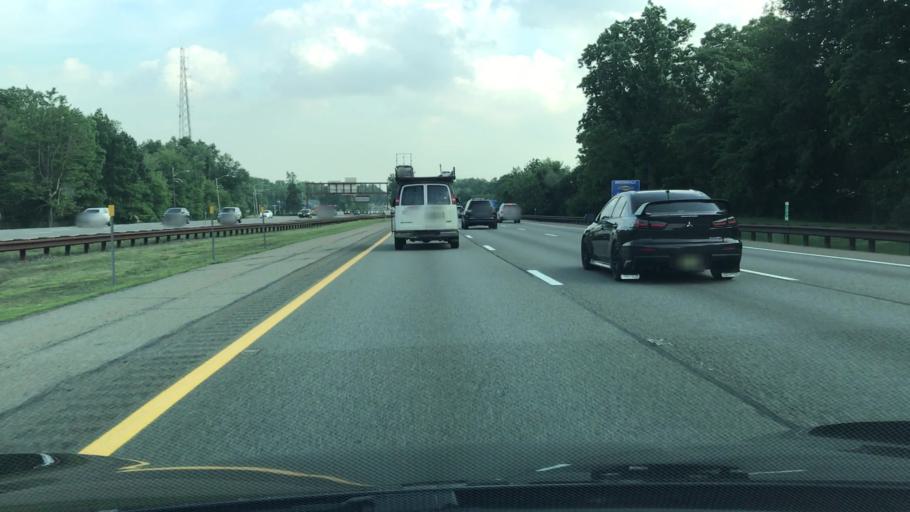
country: US
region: New Jersey
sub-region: Essex County
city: Brookdale
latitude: 40.8438
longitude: -74.1801
